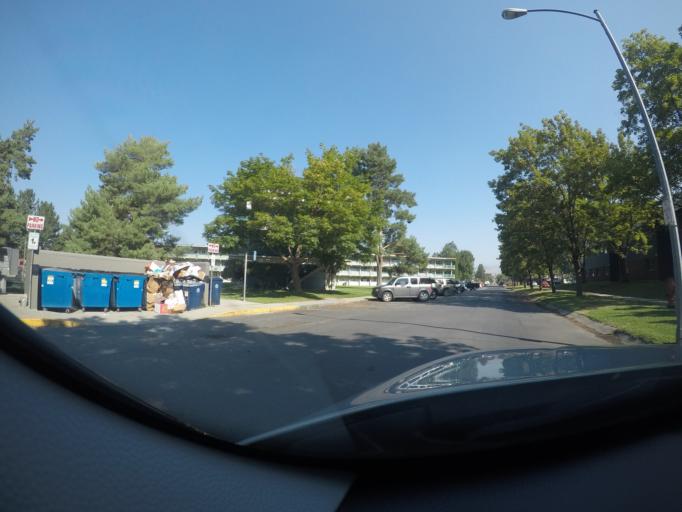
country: US
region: Montana
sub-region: Missoula County
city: Missoula
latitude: 46.8521
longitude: -113.9854
